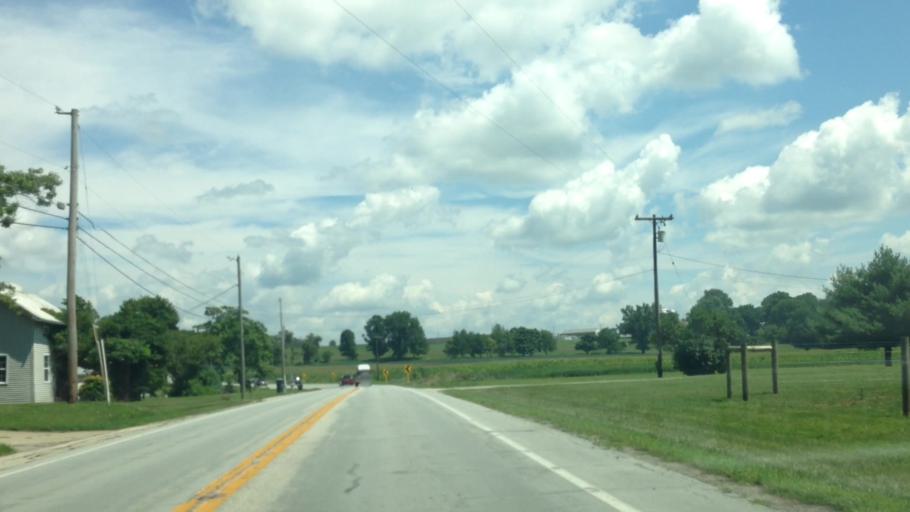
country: US
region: Ohio
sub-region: Wayne County
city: Smithville
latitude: 40.8952
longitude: -81.8103
